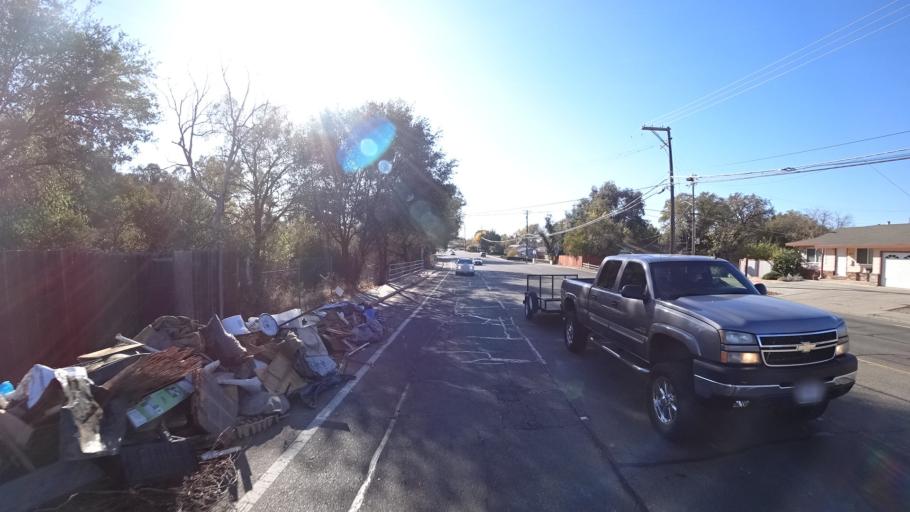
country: US
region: California
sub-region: Sacramento County
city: Antelope
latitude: 38.6760
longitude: -121.3103
